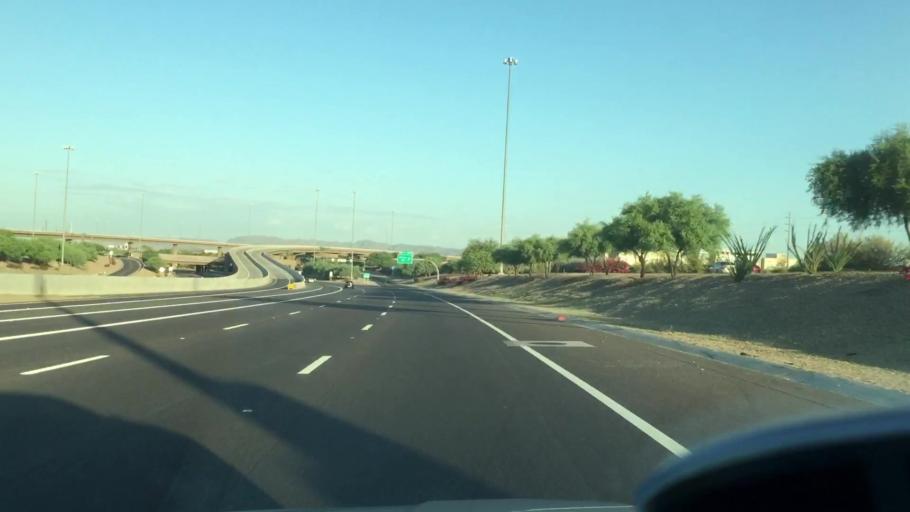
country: US
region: Arizona
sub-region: Maricopa County
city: Chandler
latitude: 33.2923
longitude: -111.8869
